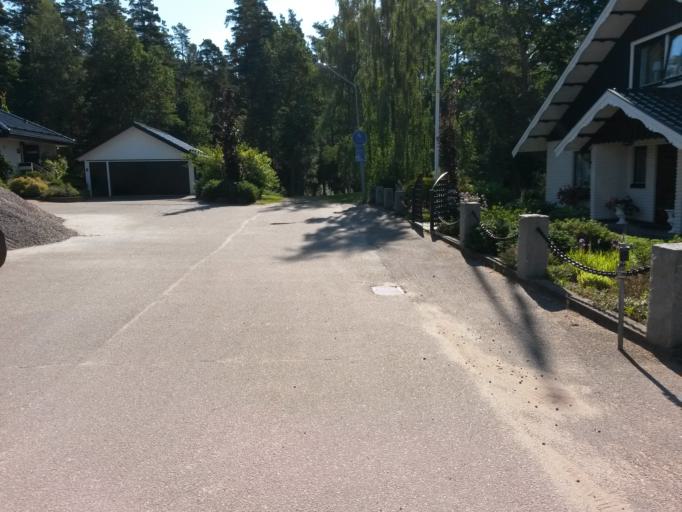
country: SE
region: Vaestra Goetaland
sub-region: Vargarda Kommun
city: Vargarda
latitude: 58.0392
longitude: 12.8231
